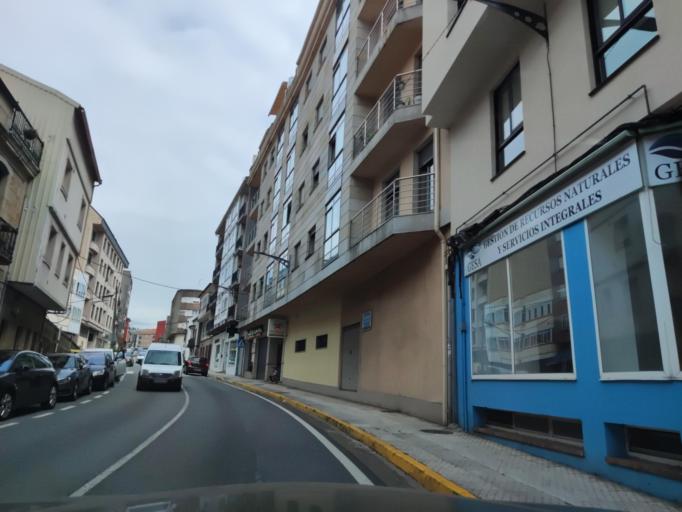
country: ES
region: Galicia
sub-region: Provincia da Coruna
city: Boiro
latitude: 42.6488
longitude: -8.8808
